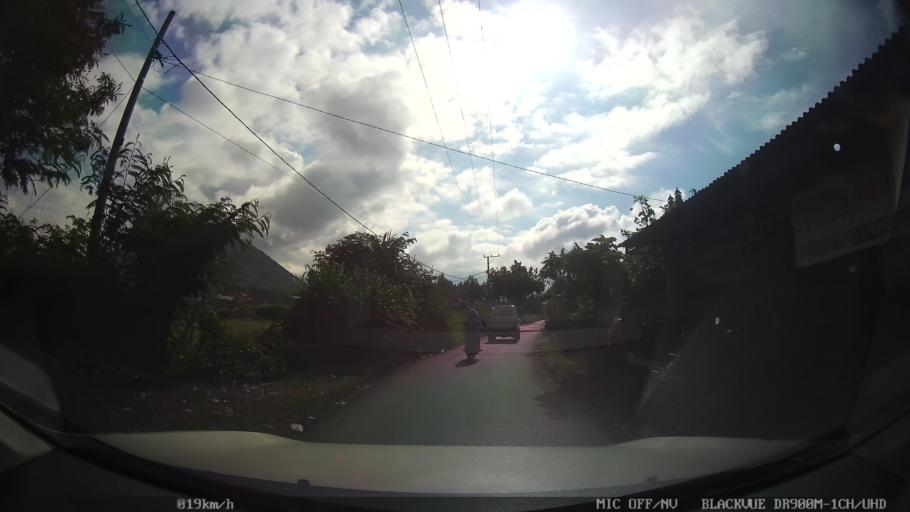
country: ID
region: Bali
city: Banjar Trunyan
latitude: -8.2254
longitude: 115.3999
